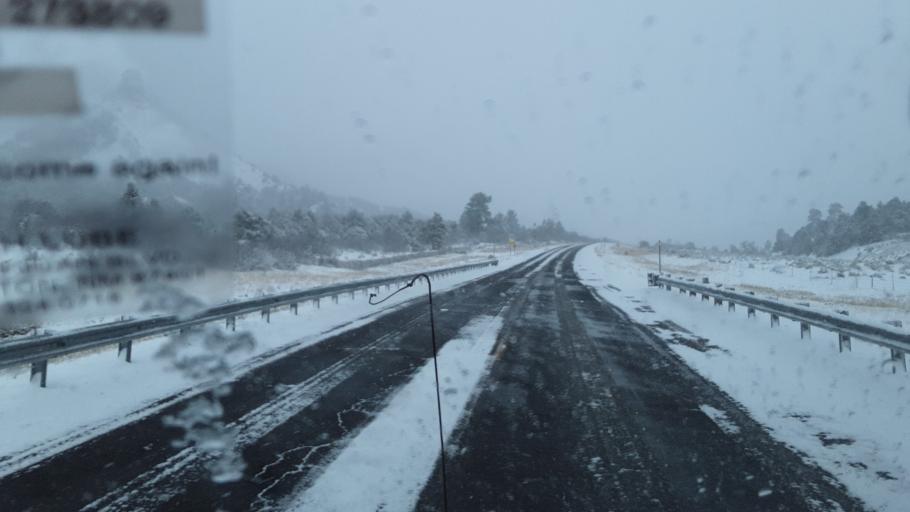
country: US
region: New Mexico
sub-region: Rio Arriba County
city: Dulce
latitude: 36.9546
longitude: -106.7885
